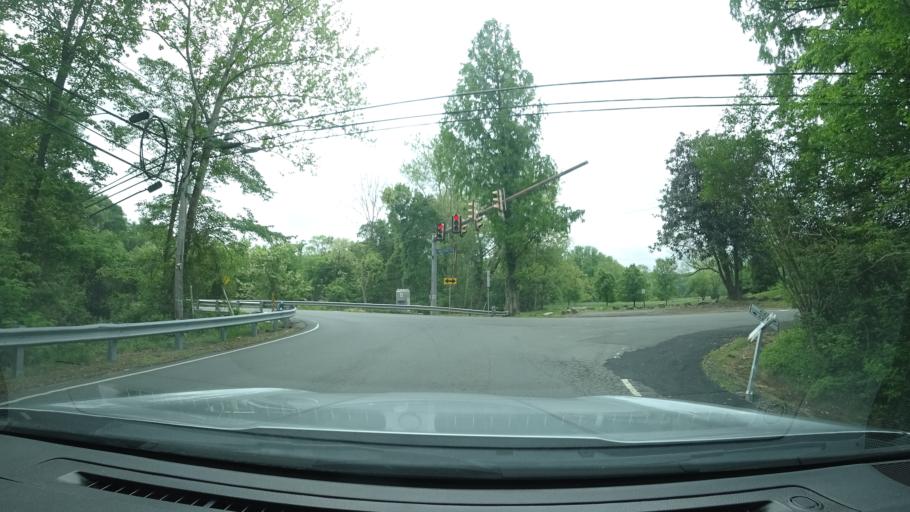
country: US
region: Virginia
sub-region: Fairfax County
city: Oakton
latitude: 38.8749
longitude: -77.3380
